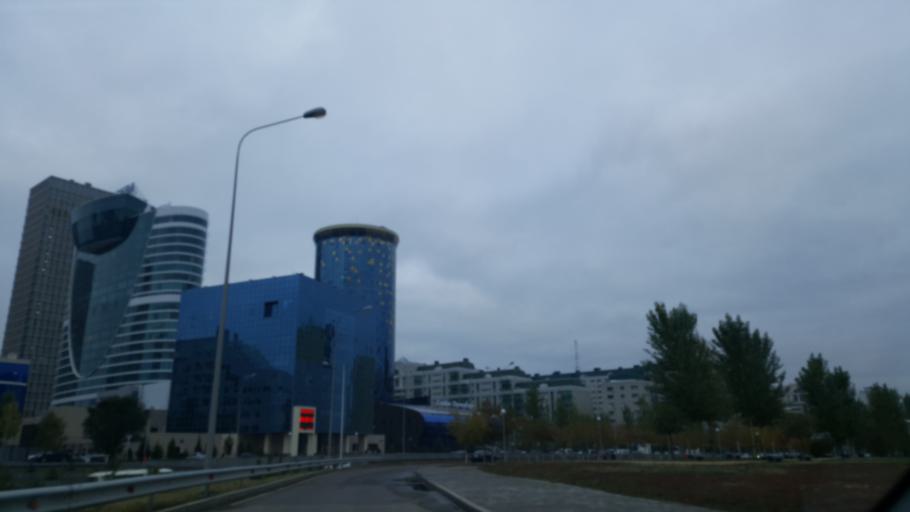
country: KZ
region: Astana Qalasy
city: Astana
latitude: 51.1228
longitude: 71.4378
